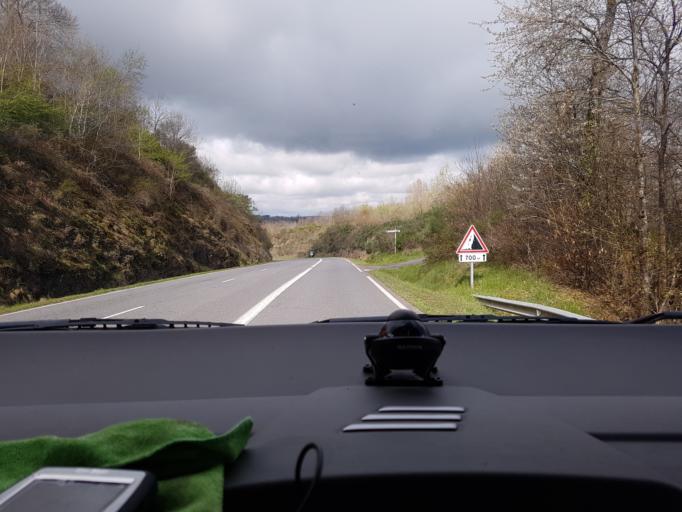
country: FR
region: Midi-Pyrenees
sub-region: Departement de l'Aveyron
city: Moyrazes
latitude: 44.3817
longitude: 2.4229
